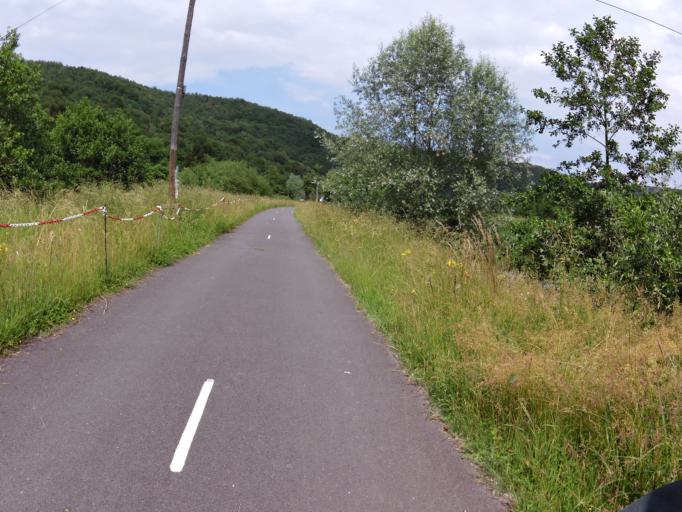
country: FR
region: Champagne-Ardenne
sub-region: Departement des Ardennes
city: Nouzonville
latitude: 49.8358
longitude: 4.7522
